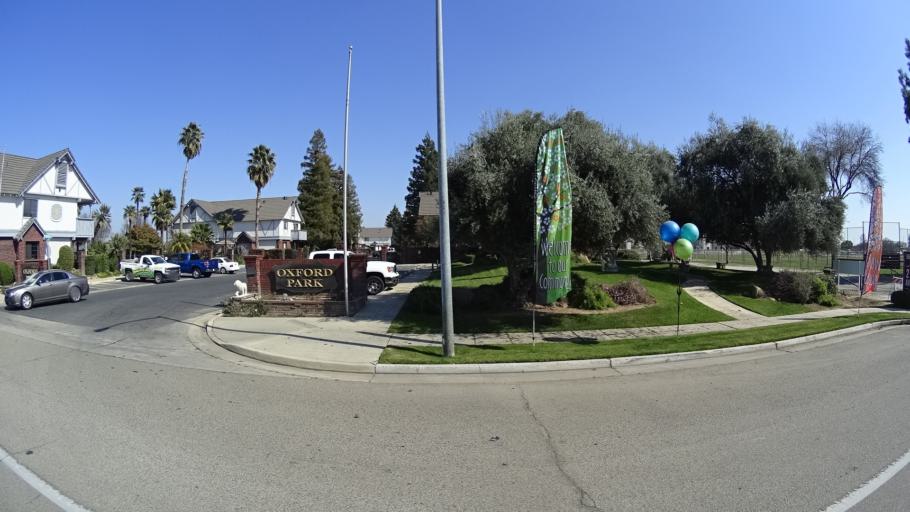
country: US
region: California
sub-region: Fresno County
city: Clovis
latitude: 36.8424
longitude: -119.7566
